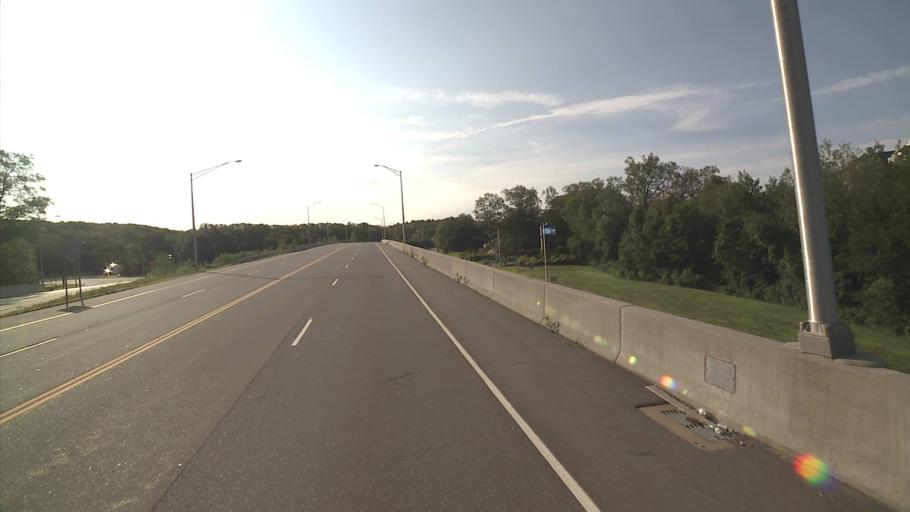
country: US
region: Connecticut
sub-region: New London County
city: Preston City
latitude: 41.4788
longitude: -71.9608
